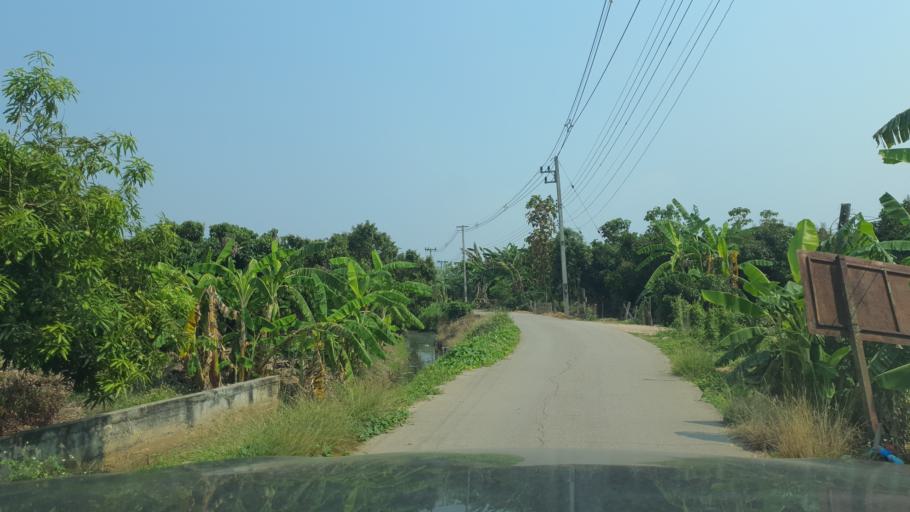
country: TH
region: Lamphun
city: Lamphun
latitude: 18.6438
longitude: 98.9901
